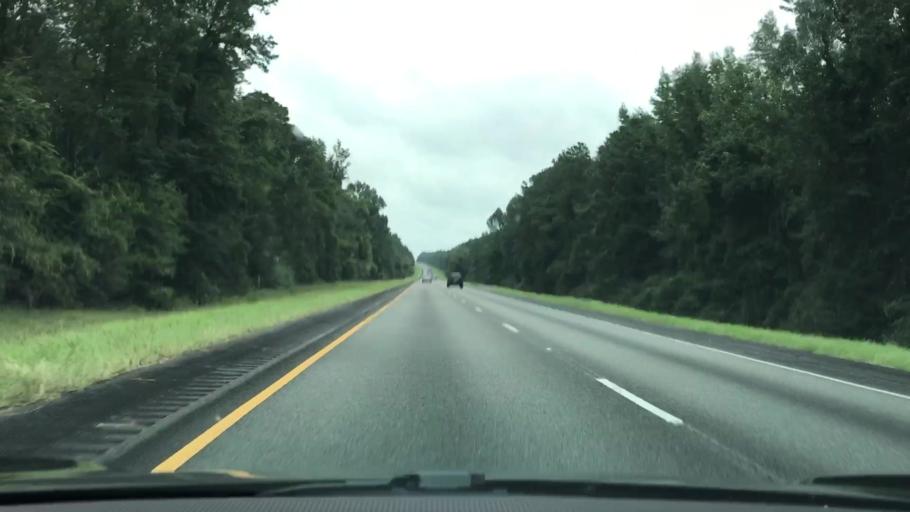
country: US
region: Alabama
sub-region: Elmore County
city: Tallassee
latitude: 32.4376
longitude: -85.8436
